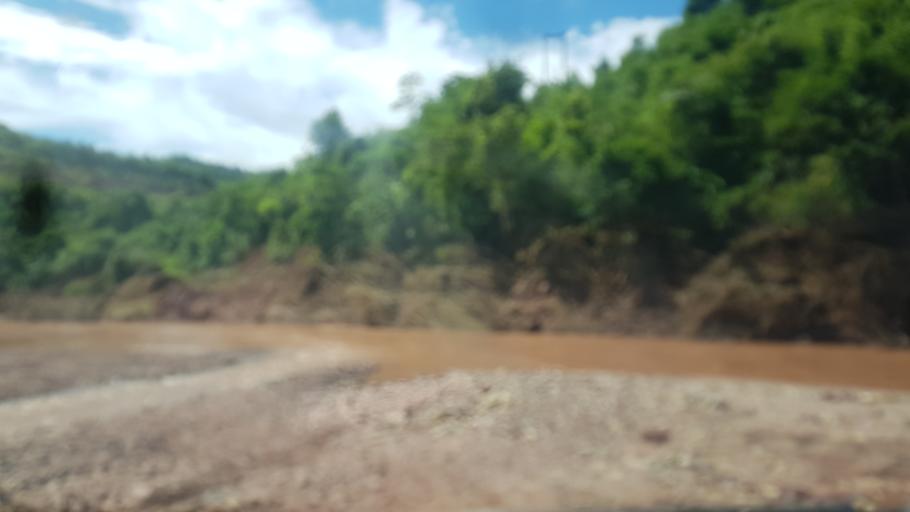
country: LA
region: Xiangkhoang
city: Phonsavan
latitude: 19.7596
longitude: 103.0166
